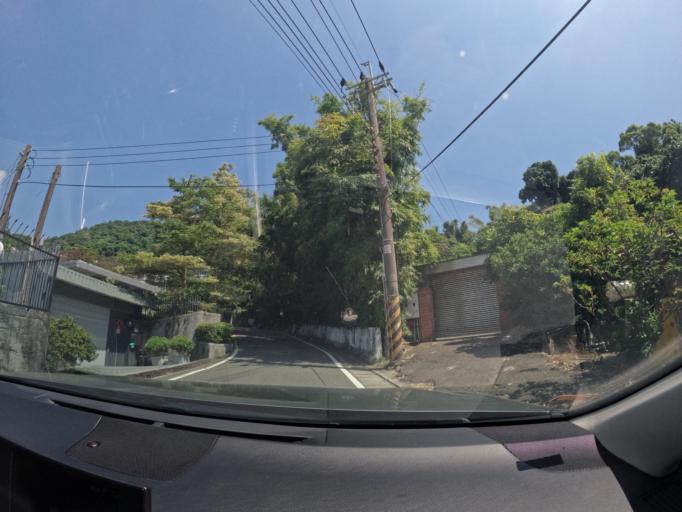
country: TW
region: Taipei
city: Taipei
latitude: 25.1186
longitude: 121.5423
